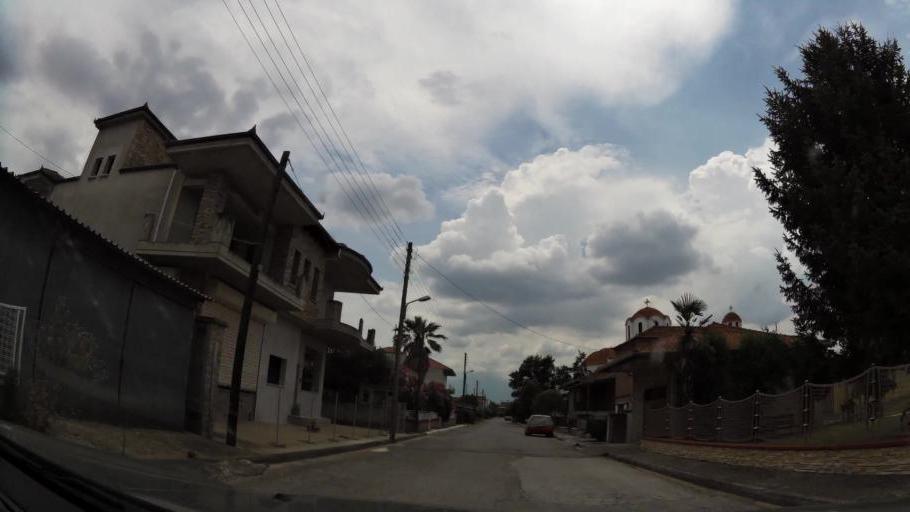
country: GR
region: Central Macedonia
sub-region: Nomos Pierias
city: Kallithea
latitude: 40.2740
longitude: 22.5776
